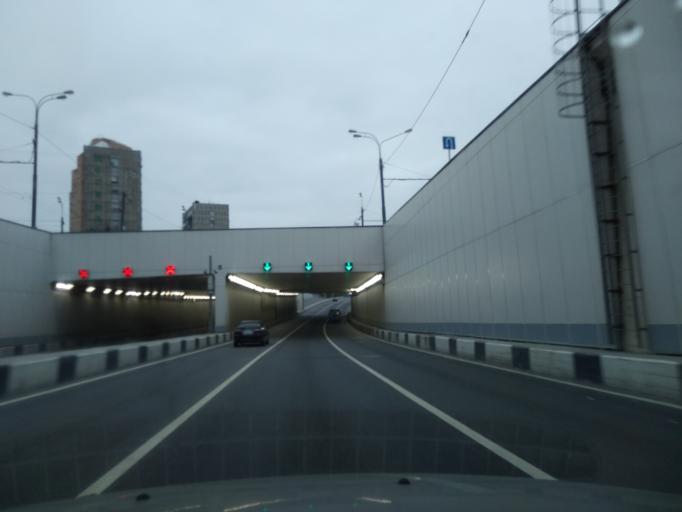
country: RU
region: Moskovskaya
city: Koptevo
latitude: 55.8360
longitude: 37.5379
